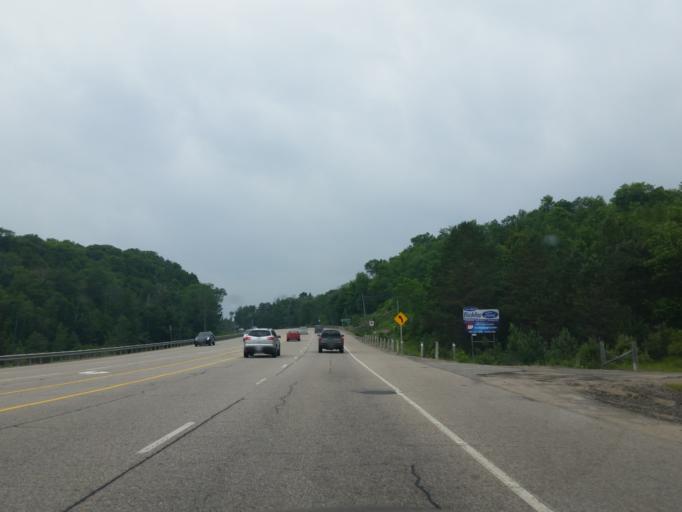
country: CA
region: Ontario
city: Huntsville
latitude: 45.3441
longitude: -79.1615
